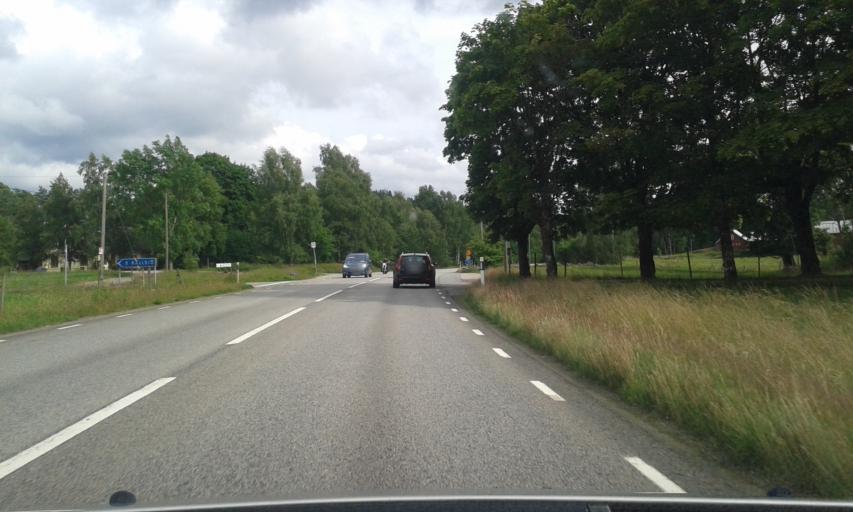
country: SE
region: Vaestra Goetaland
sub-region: Marks Kommun
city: Horred
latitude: 57.1483
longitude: 12.6862
